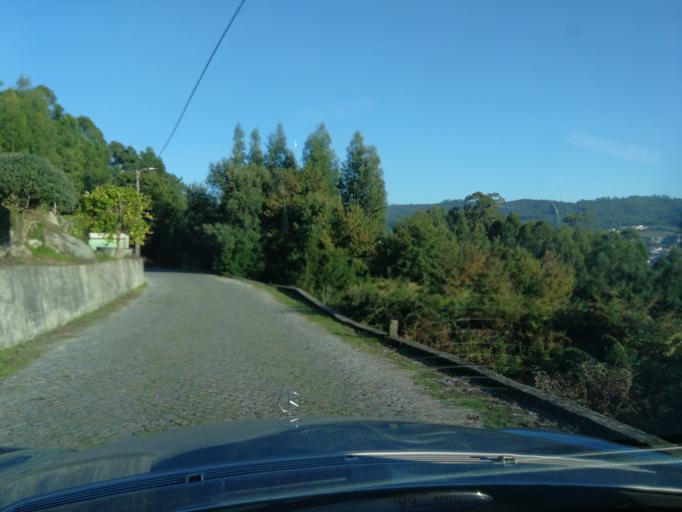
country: PT
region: Braga
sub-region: Braga
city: Oliveira
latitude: 41.4540
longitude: -8.4652
